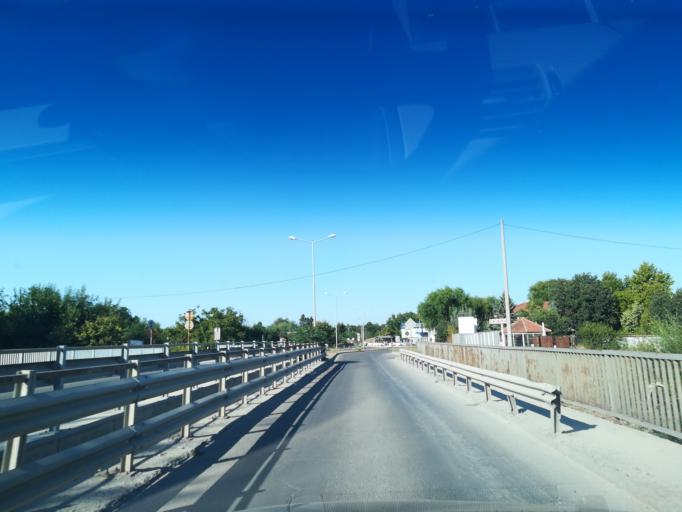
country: BG
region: Plovdiv
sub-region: Obshtina Plovdiv
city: Plovdiv
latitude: 42.1642
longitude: 24.7741
